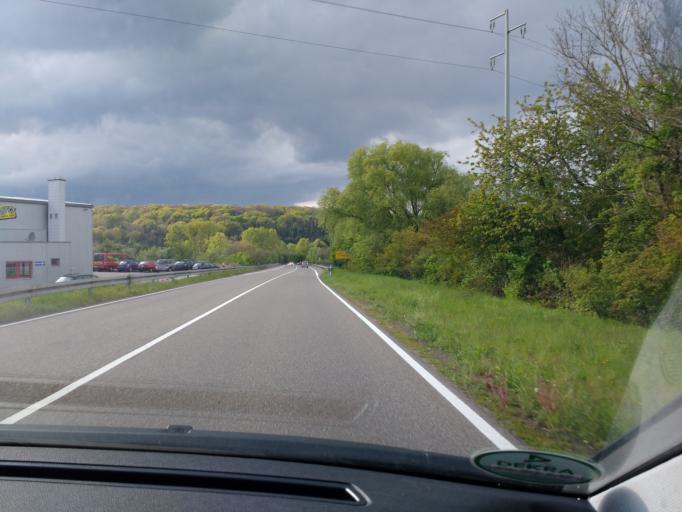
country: DE
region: Saarland
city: Kleinblittersdorf
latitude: 49.1693
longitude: 7.0317
